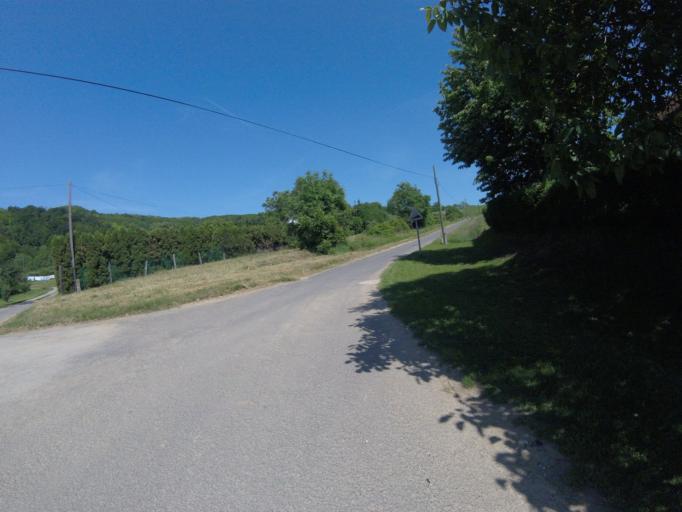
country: HU
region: Zala
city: Zalaszentgrot
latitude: 46.9218
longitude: 17.0534
